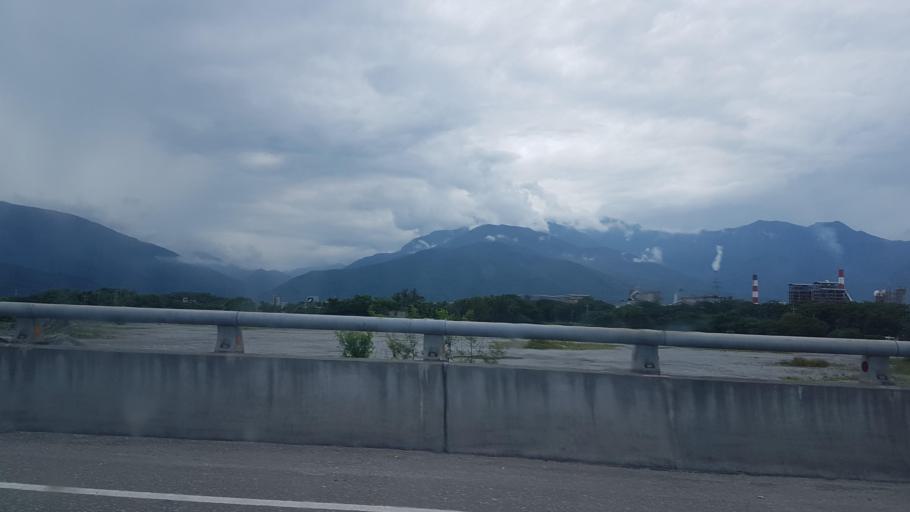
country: TW
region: Taiwan
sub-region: Hualien
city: Hualian
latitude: 23.9222
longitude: 121.5874
